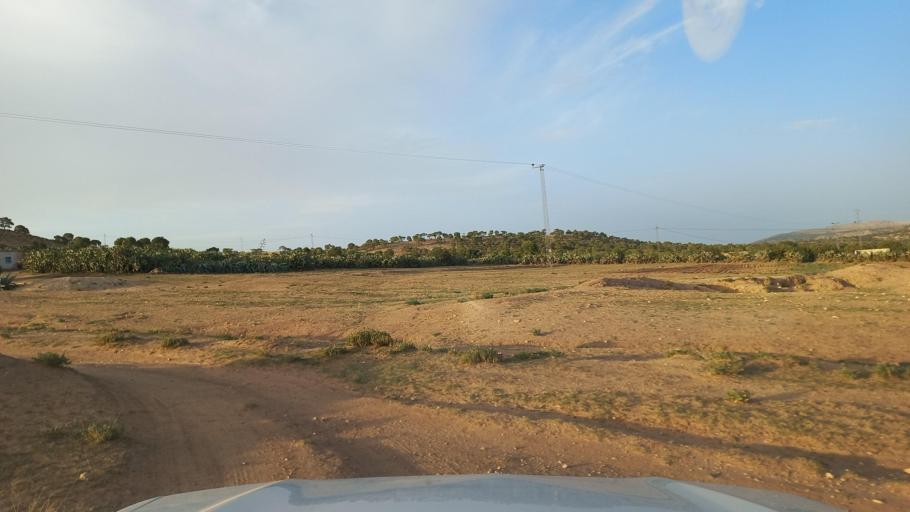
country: TN
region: Al Qasrayn
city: Sbiba
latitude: 35.4114
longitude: 8.9084
